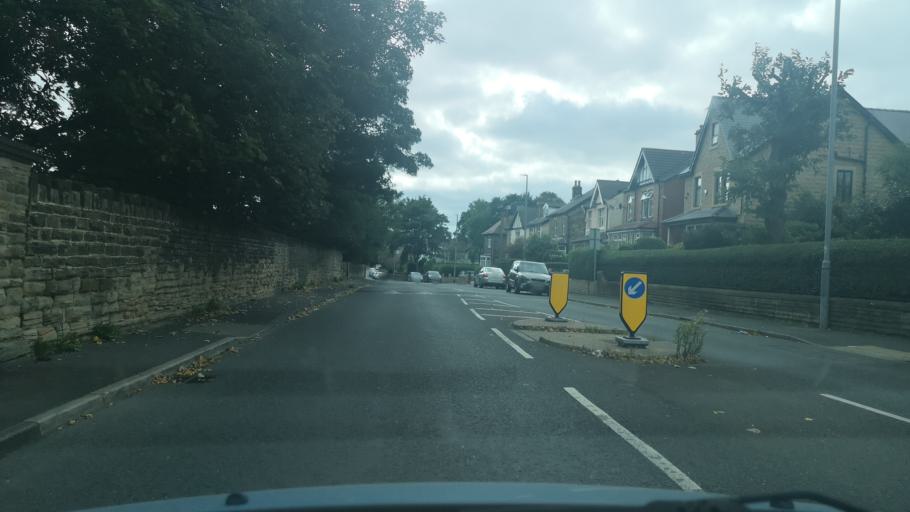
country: GB
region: England
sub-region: Kirklees
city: Batley
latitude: 53.7067
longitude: -1.6414
